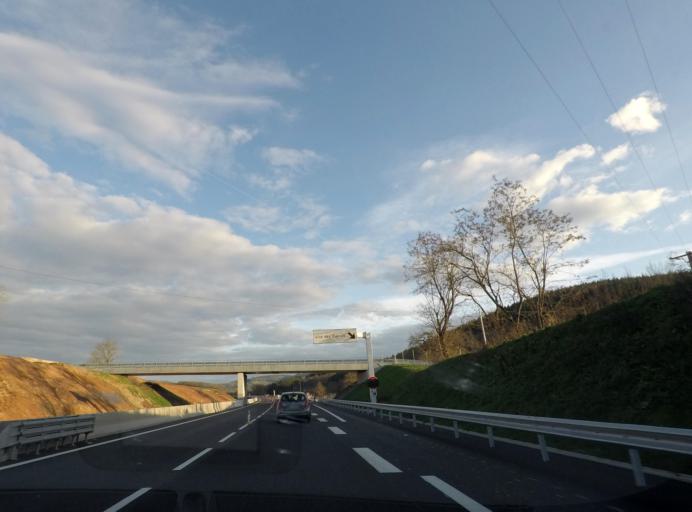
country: FR
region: Bourgogne
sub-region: Departement de Saone-et-Loire
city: Matour
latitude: 46.3736
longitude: 4.5381
